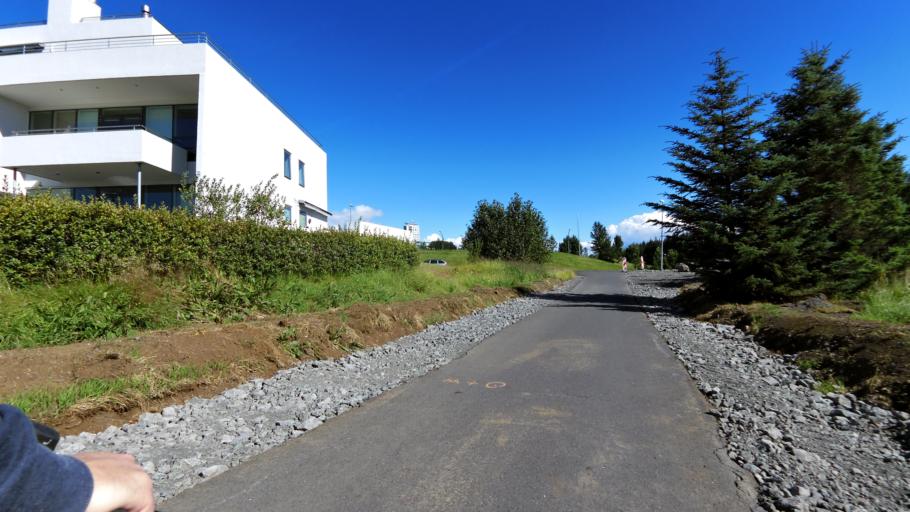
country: IS
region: Capital Region
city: Kopavogur
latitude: 64.1204
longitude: -21.9011
